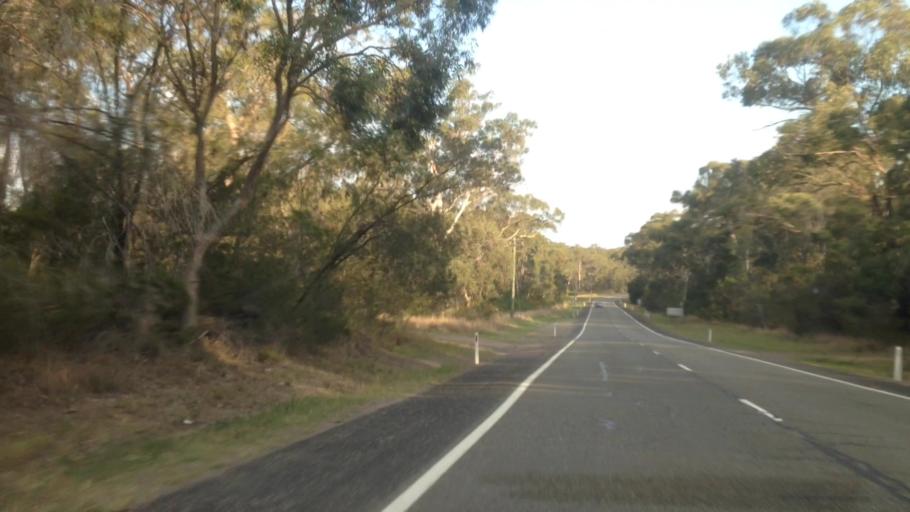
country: AU
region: New South Wales
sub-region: Cessnock
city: Kurri Kurri
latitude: -32.8357
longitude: 151.4814
